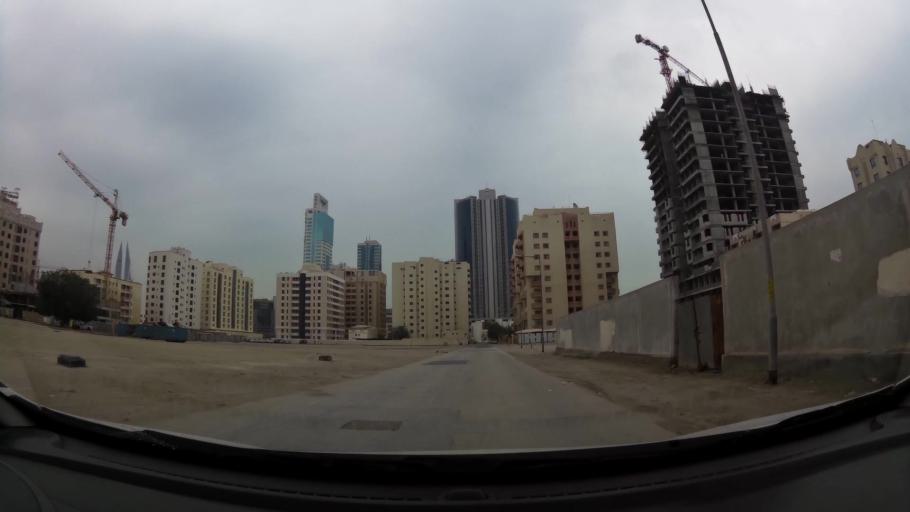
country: BH
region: Manama
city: Manama
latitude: 26.2376
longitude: 50.5944
